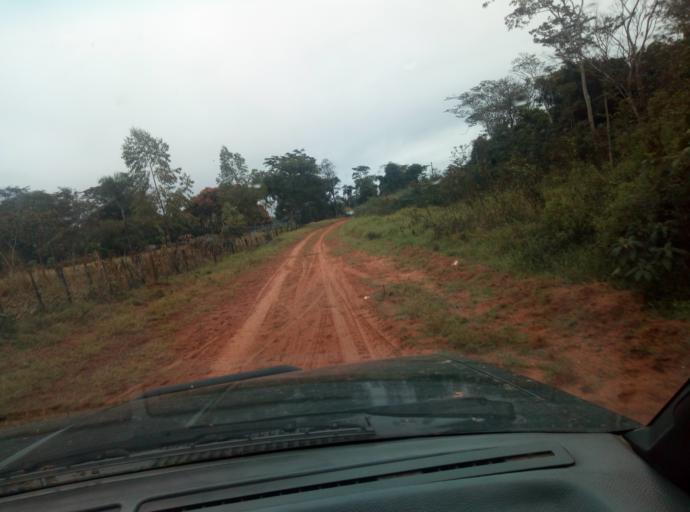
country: PY
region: Caaguazu
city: Carayao
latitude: -25.1916
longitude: -56.3431
